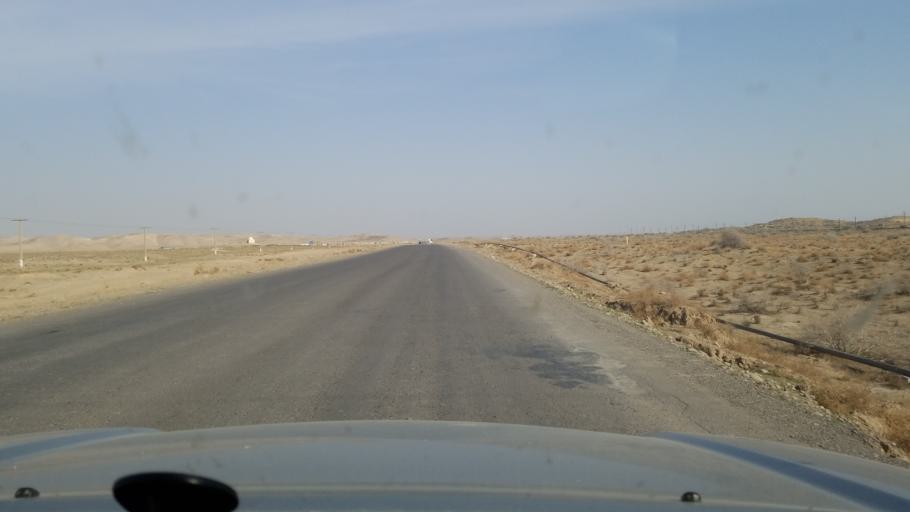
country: AF
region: Jowzjan
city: Khamyab
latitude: 37.7052
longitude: 65.5505
